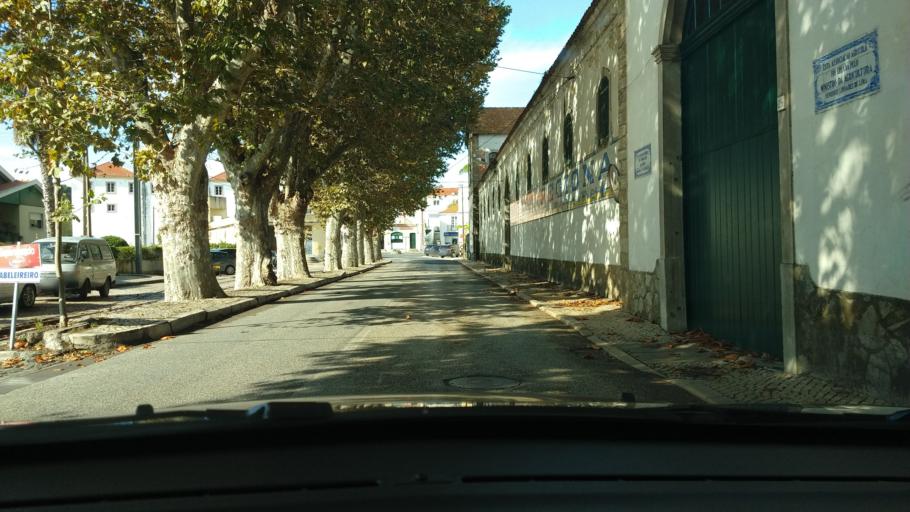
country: PT
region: Lisbon
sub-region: Sintra
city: Colares
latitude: 38.8052
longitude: -9.4498
